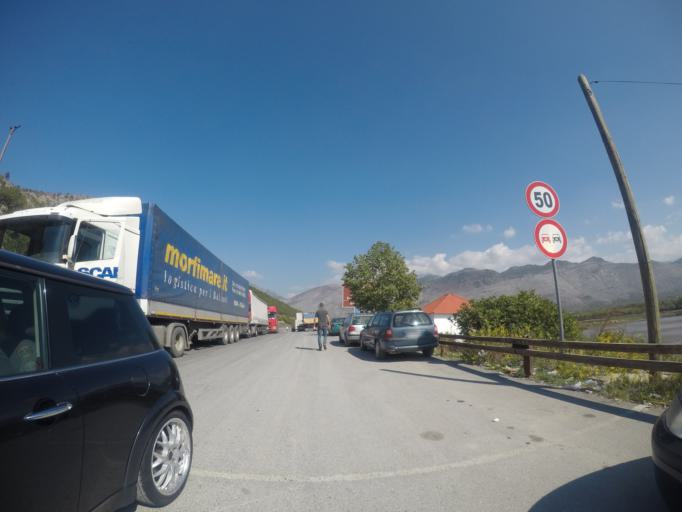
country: AL
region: Shkoder
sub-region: Rrethi i Malesia e Madhe
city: Hot
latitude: 42.3313
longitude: 19.4220
